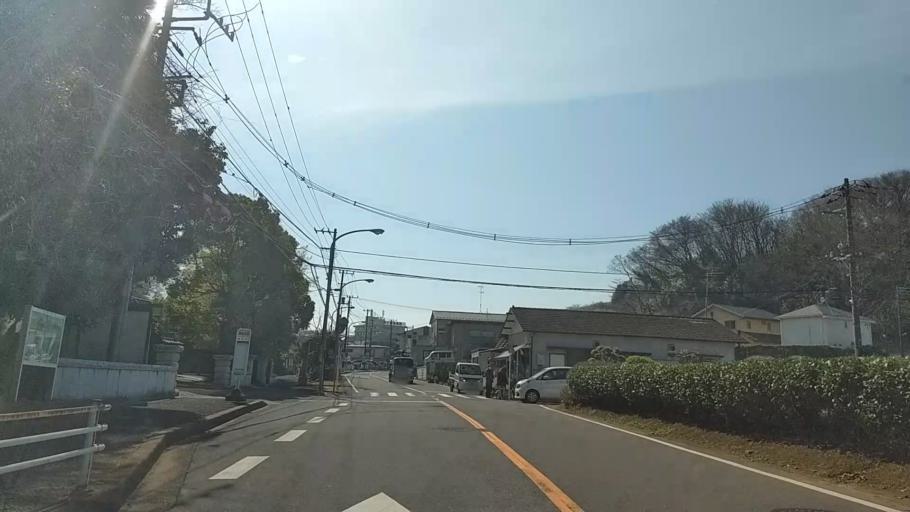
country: JP
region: Kanagawa
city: Kamakura
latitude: 35.3995
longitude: 139.5554
